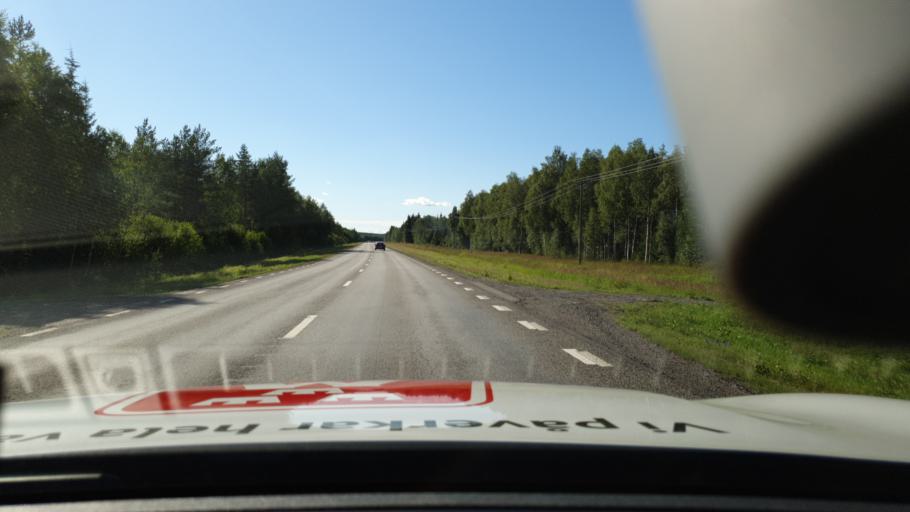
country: SE
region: Norrbotten
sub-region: Pitea Kommun
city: Rosvik
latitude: 65.5755
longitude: 21.7308
